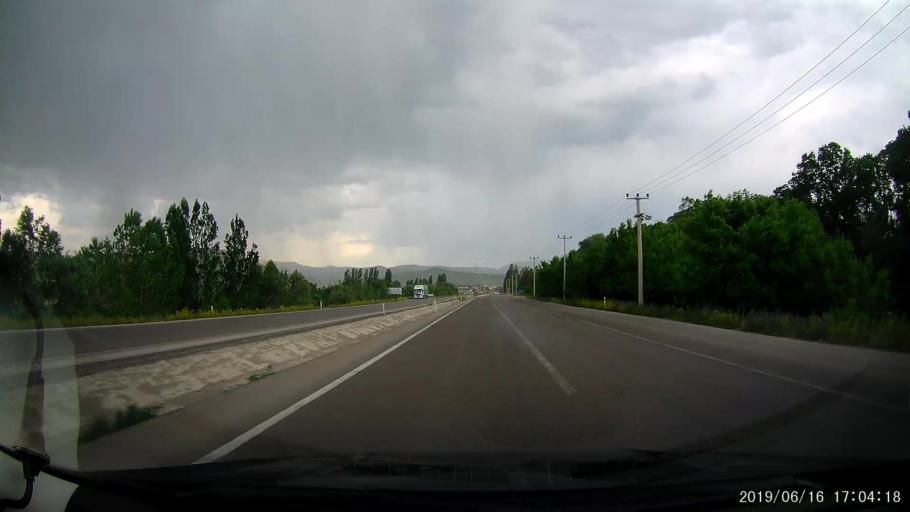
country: TR
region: Erzurum
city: Askale
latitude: 39.9272
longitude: 40.7119
